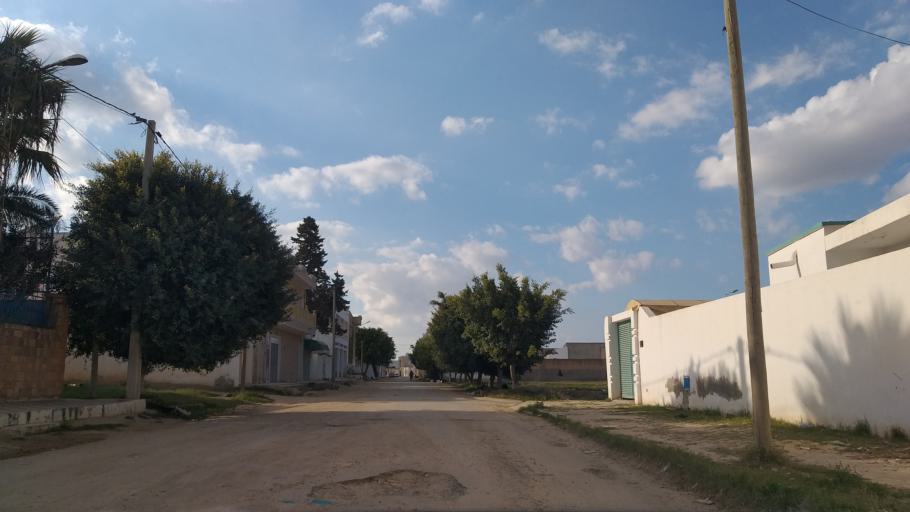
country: TN
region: Al Mahdiyah
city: El Jem
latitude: 35.3037
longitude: 10.7022
